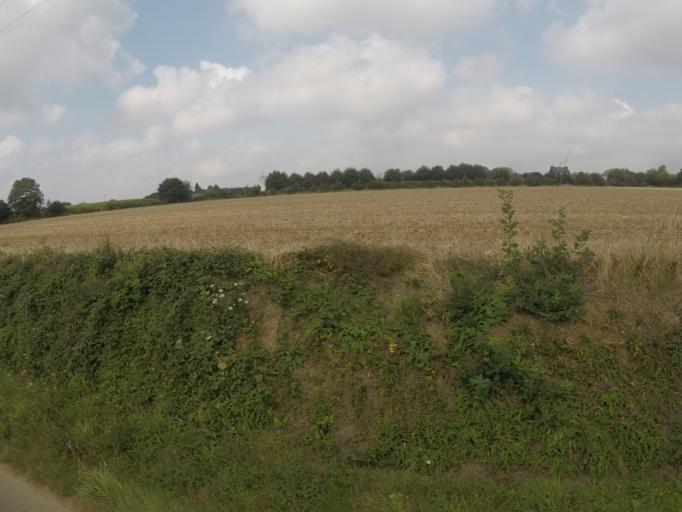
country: FR
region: Brittany
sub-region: Departement des Cotes-d'Armor
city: Plelo
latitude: 48.5565
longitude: -2.9357
